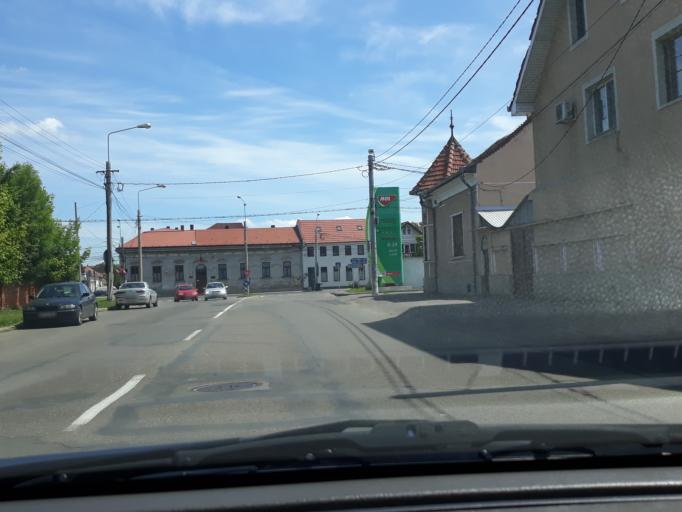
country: RO
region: Bihor
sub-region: Comuna Biharea
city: Oradea
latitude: 47.0519
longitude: 21.9180
